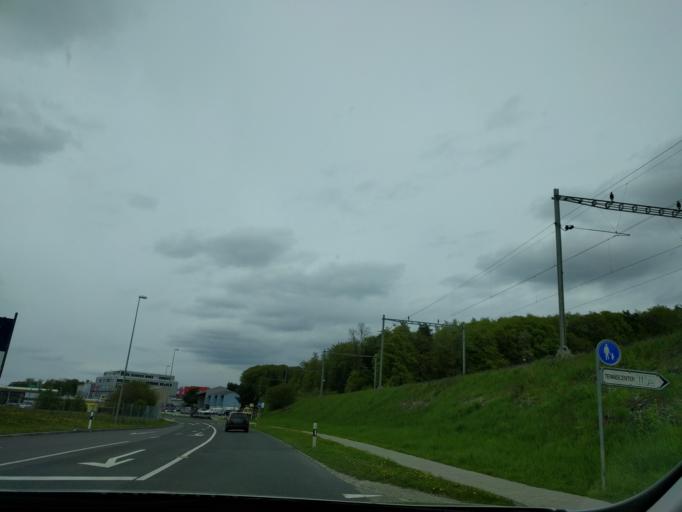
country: CH
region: Fribourg
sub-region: Sense District
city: Dudingen
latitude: 46.8569
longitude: 7.1996
